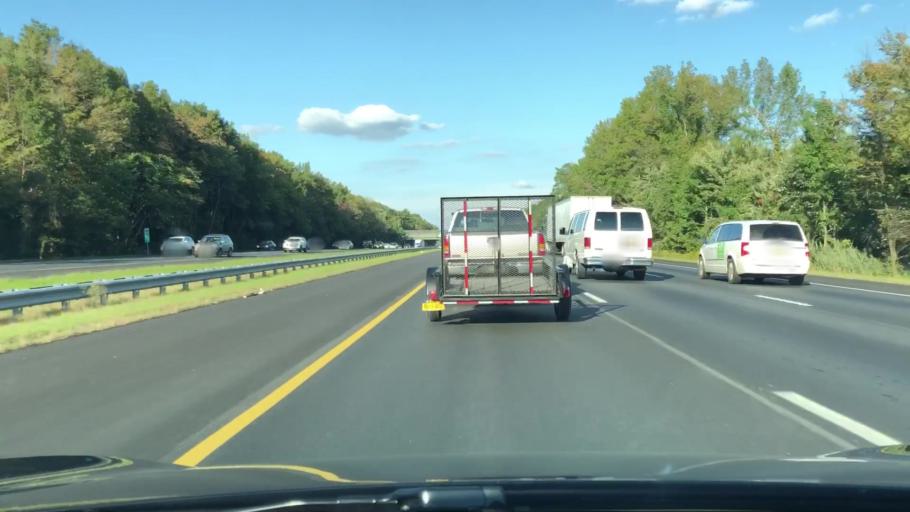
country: US
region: New Jersey
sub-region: Burlington County
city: Ramblewood
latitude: 39.9535
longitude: -74.9256
